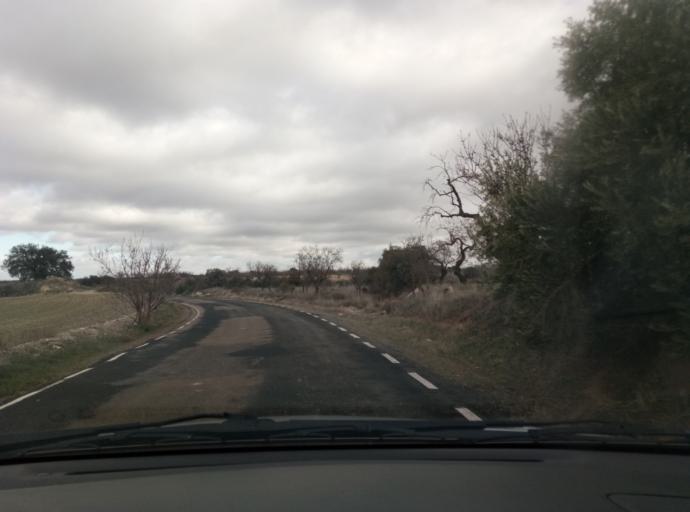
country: ES
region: Catalonia
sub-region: Provincia de Lleida
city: Vallbona de les Monges
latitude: 41.5729
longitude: 1.0731
